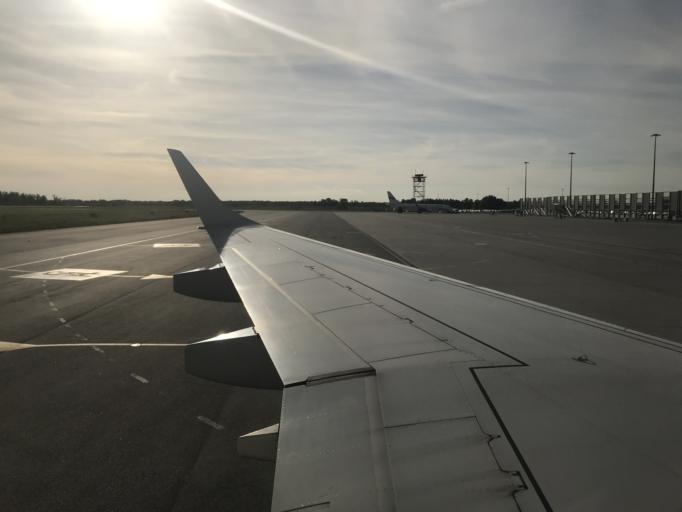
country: PL
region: Lower Silesian Voivodeship
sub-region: Powiat wroclawski
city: Smolec
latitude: 51.1083
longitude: 16.8789
